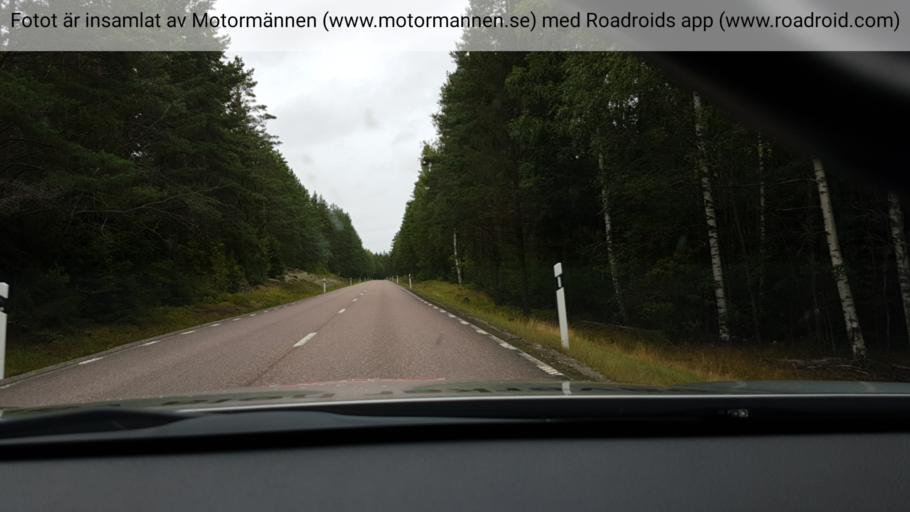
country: SE
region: Gaevleborg
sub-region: Gavle Kommun
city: Hedesunda
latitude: 60.3229
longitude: 16.9182
